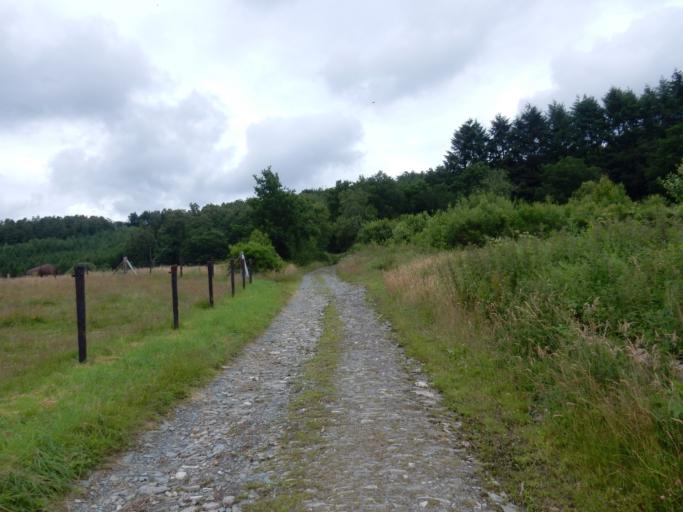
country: BE
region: Wallonia
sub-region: Province de Namur
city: Bievre
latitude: 49.8597
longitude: 4.9584
